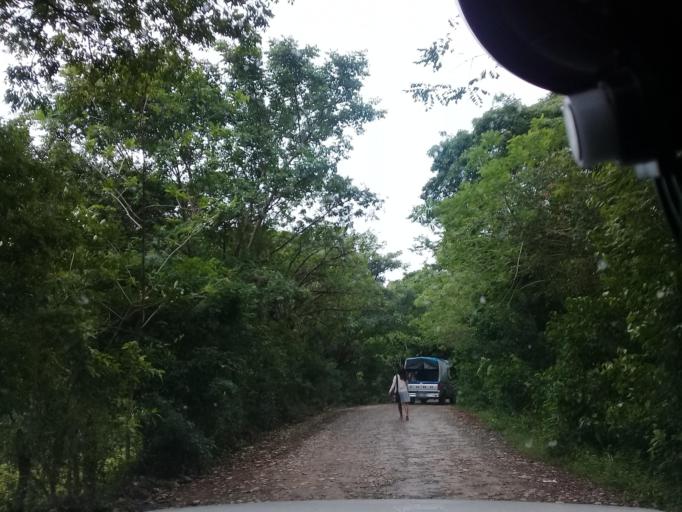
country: MX
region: Veracruz
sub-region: Chalma
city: San Pedro Coyutla
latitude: 21.2321
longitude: -98.4204
